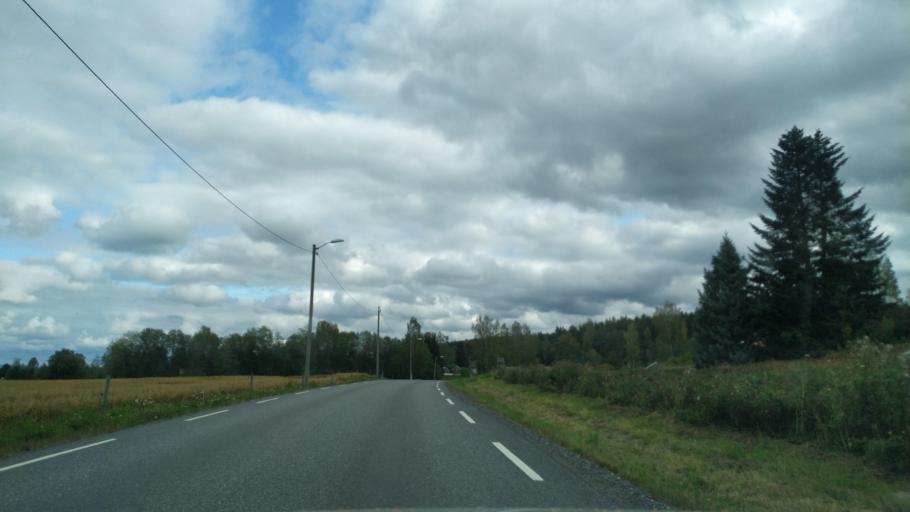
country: NO
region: Akershus
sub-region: Nes
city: Auli
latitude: 60.0571
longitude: 11.4185
